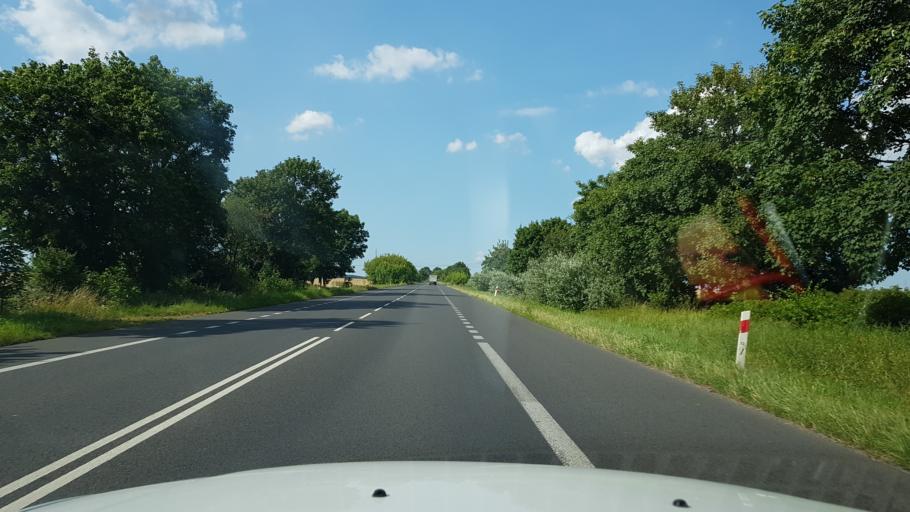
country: PL
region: West Pomeranian Voivodeship
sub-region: Powiat gryfinski
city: Stare Czarnowo
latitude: 53.2599
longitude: 14.7846
